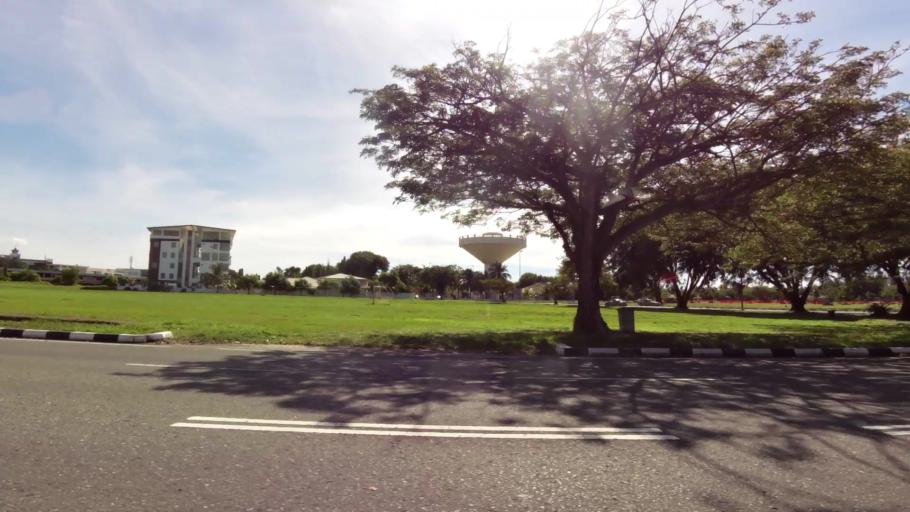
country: BN
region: Belait
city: Kuala Belait
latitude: 4.5861
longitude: 114.2025
